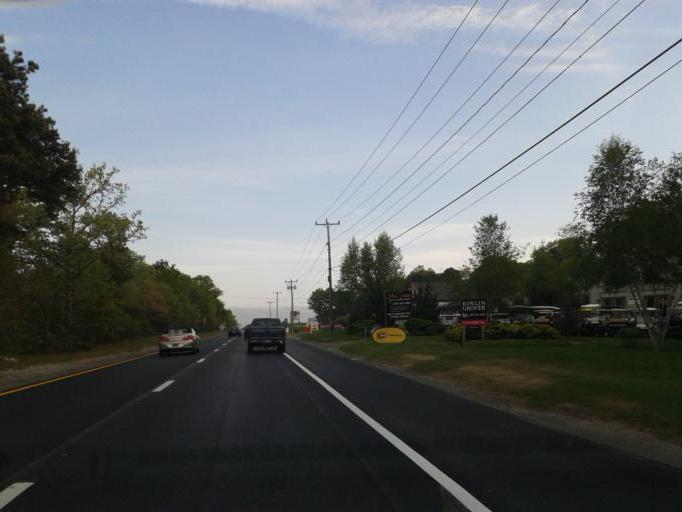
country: US
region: Massachusetts
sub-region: Barnstable County
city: Pocasset
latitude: 41.6917
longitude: -70.5888
